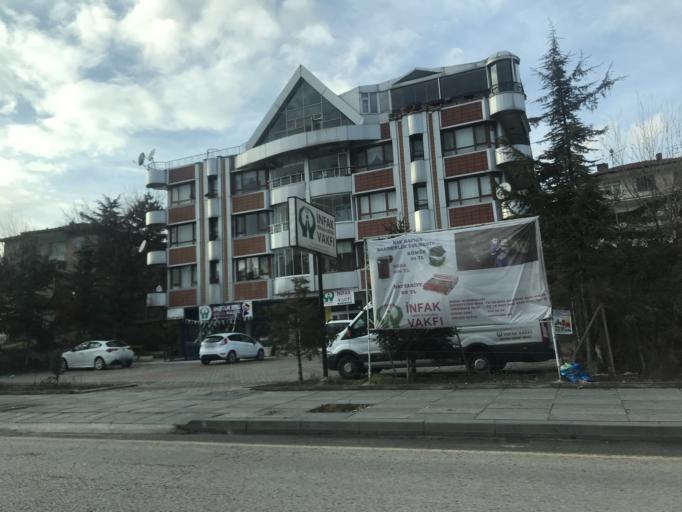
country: TR
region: Ankara
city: Mamak
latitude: 39.9842
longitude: 32.8945
